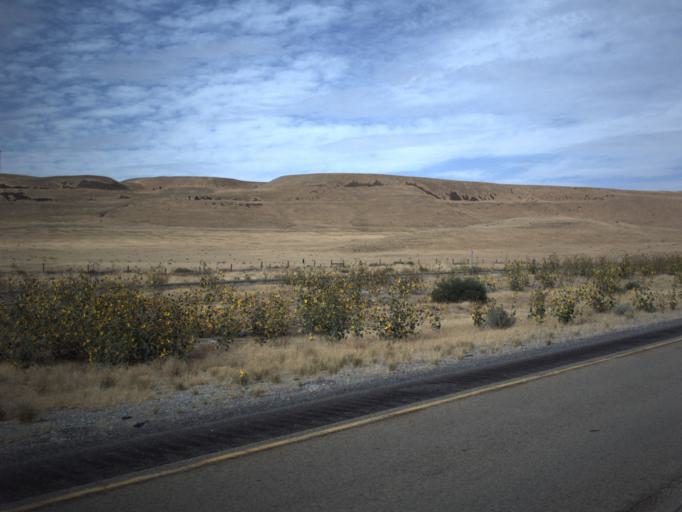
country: US
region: Utah
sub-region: Tooele County
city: Grantsville
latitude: 40.8086
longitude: -112.8647
